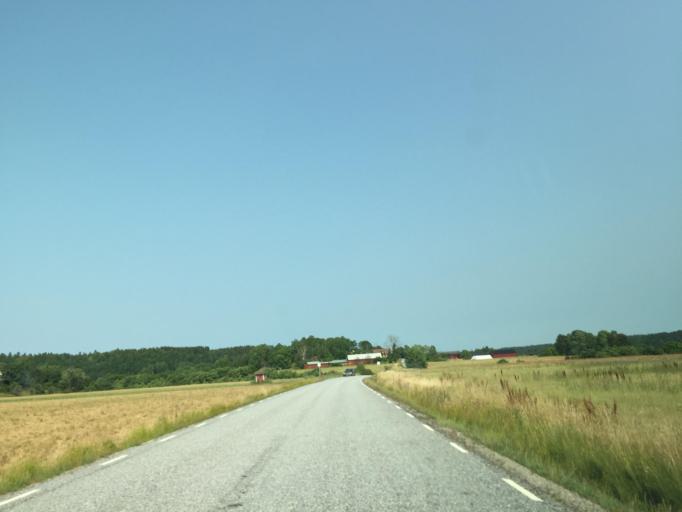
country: SE
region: Vaestra Goetaland
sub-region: Lilla Edets Kommun
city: Lilla Edet
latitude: 58.2074
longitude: 12.1288
